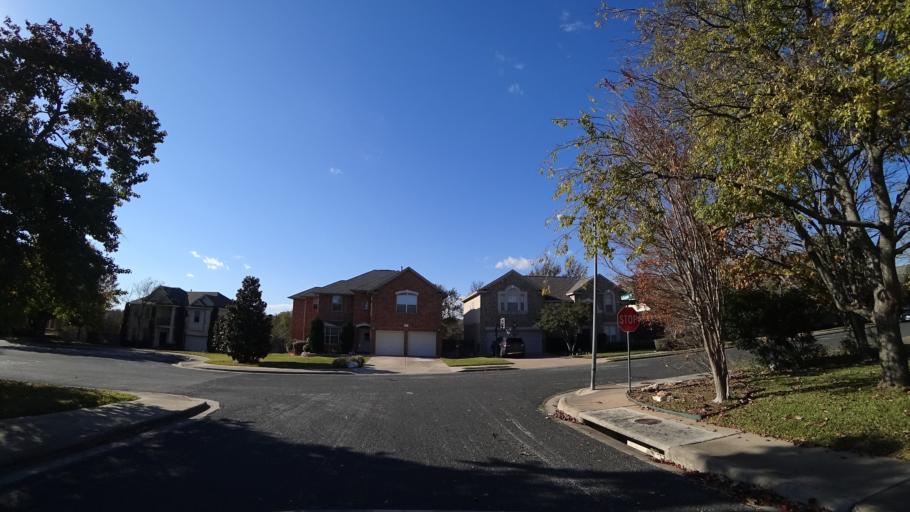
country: US
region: Texas
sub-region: Williamson County
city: Brushy Creek
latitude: 30.4869
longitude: -97.7373
